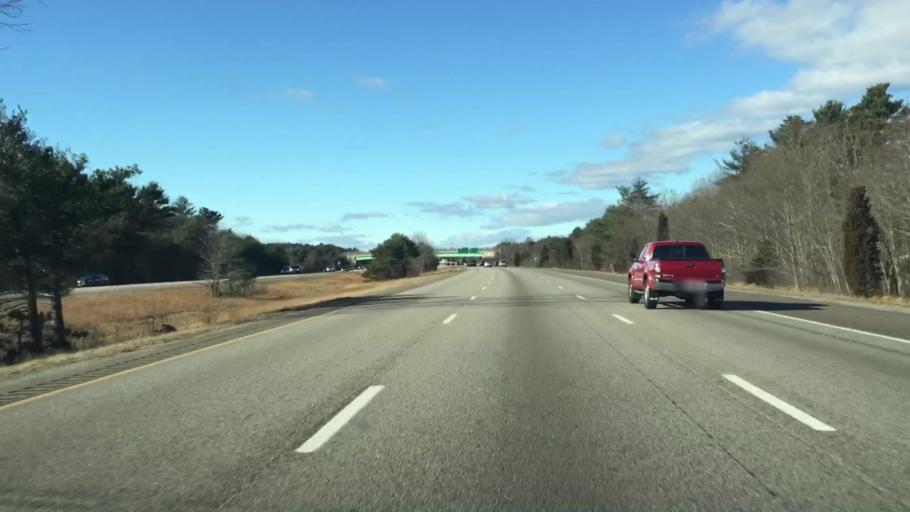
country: US
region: Massachusetts
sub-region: Bristol County
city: Mansfield Center
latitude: 42.0219
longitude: -71.2467
